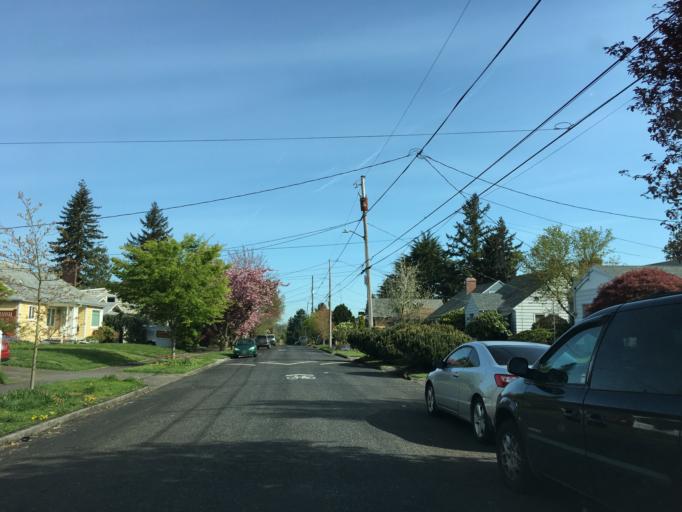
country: US
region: Oregon
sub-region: Multnomah County
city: Lents
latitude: 45.5233
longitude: -122.5751
